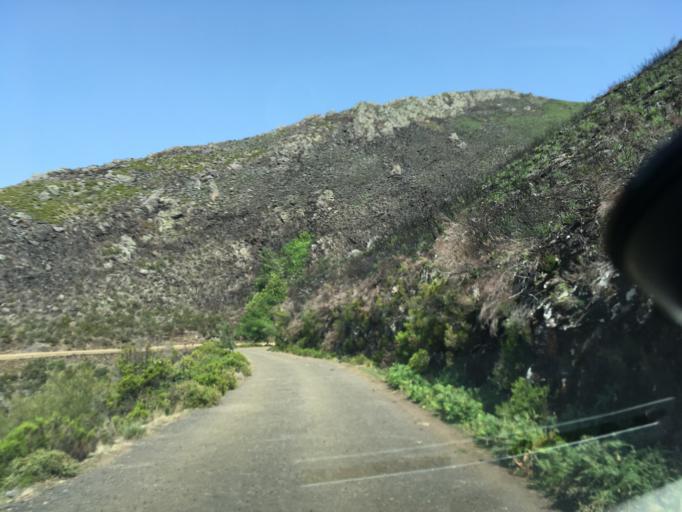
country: PT
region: Braga
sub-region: Celorico de Basto
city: Celorico de Basto
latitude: 41.2871
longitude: -7.9382
